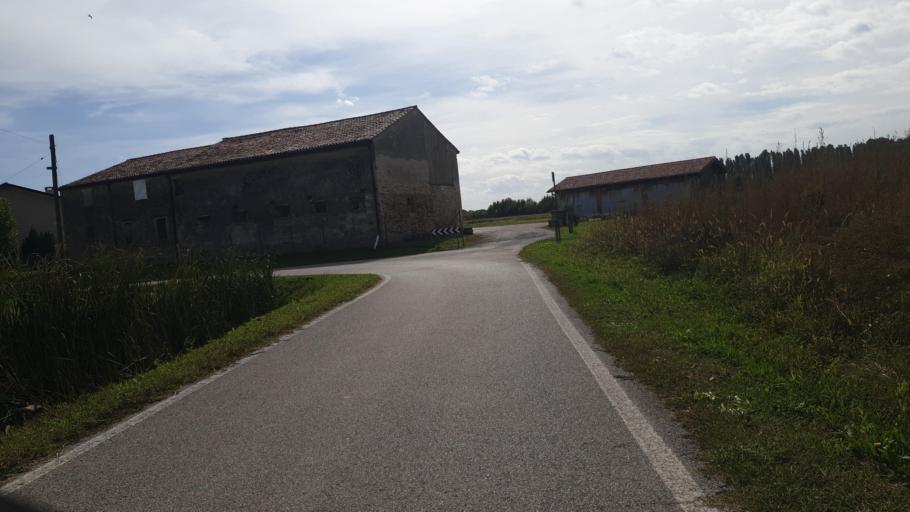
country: IT
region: Veneto
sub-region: Provincia di Padova
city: Brugine
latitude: 45.2968
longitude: 11.9742
